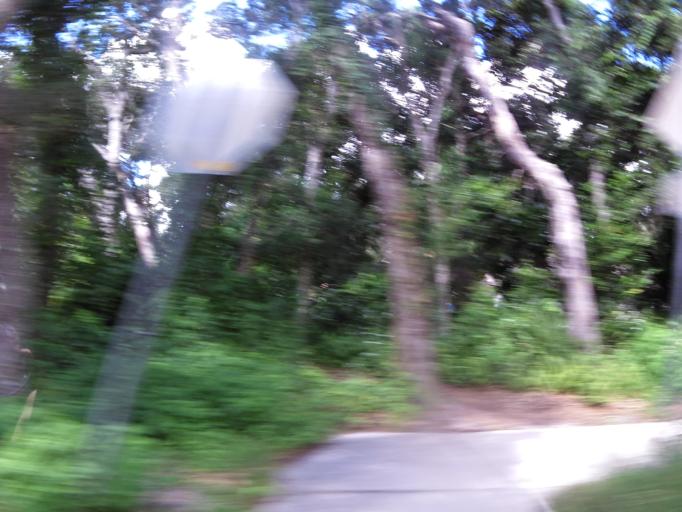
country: US
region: Florida
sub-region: Nassau County
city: Fernandina Beach
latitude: 30.5871
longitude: -81.4465
